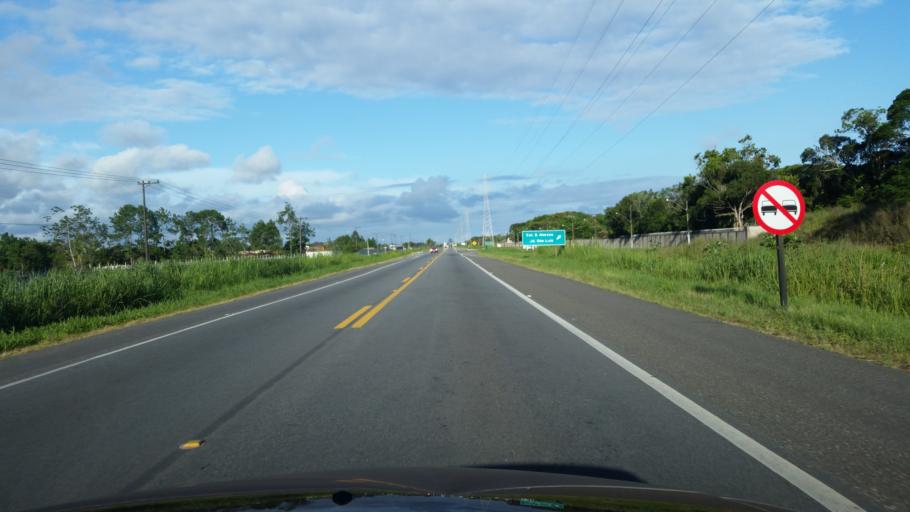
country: BR
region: Sao Paulo
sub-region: Peruibe
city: Peruibe
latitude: -24.2768
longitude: -46.9813
